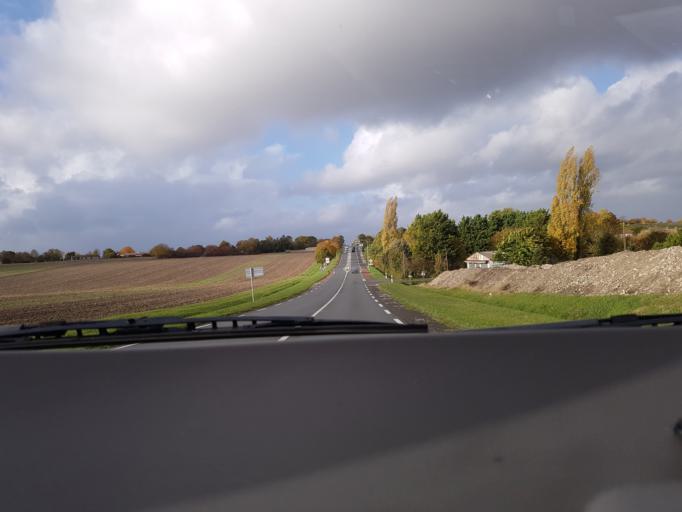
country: FR
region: Poitou-Charentes
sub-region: Departement de la Charente-Maritime
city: Thenac
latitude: 45.6486
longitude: -0.5847
